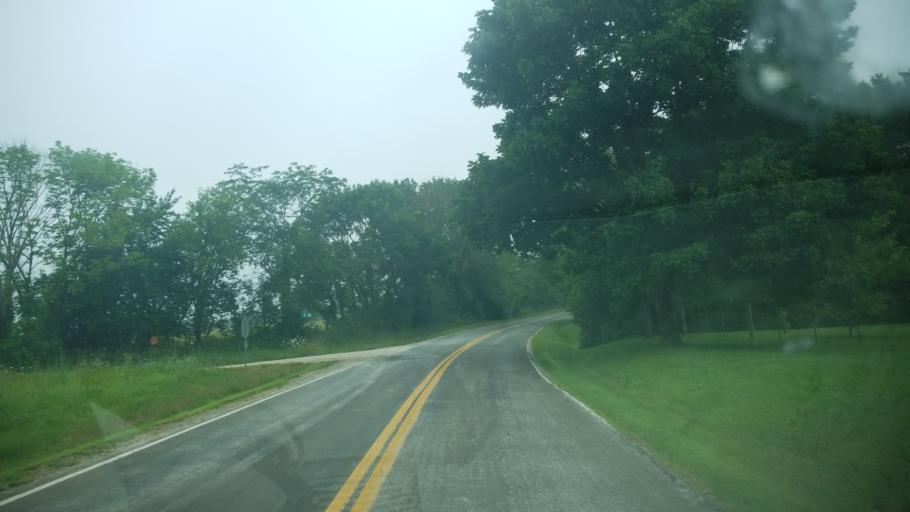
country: US
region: Missouri
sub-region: Audrain County
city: Vandalia
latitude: 39.3018
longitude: -91.3502
